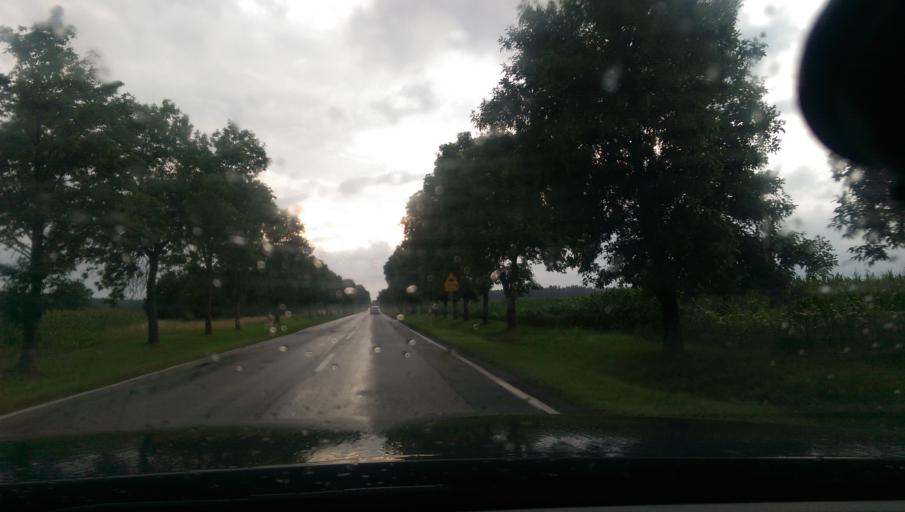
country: PL
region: Warmian-Masurian Voivodeship
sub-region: Powiat szczycienski
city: Swietajno
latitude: 53.5538
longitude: 21.1489
